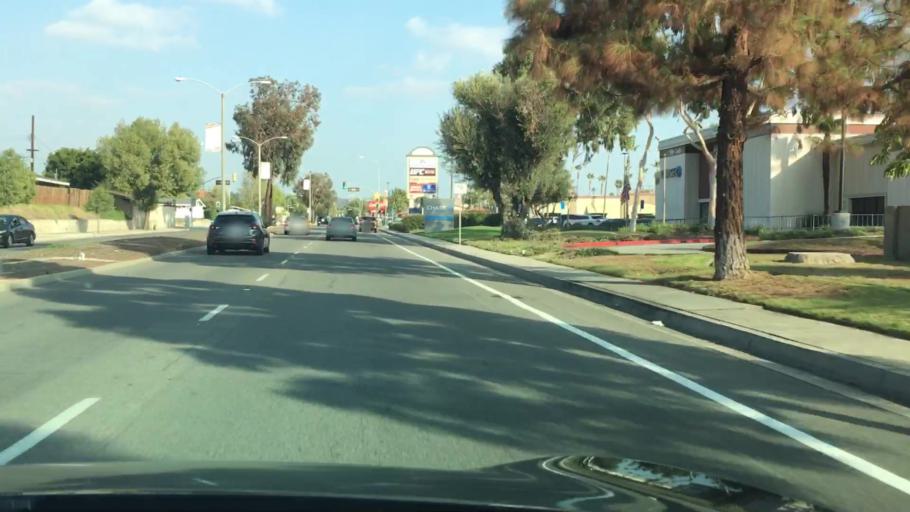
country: US
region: California
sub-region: Los Angeles County
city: La Mirada
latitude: 33.8985
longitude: -118.0088
